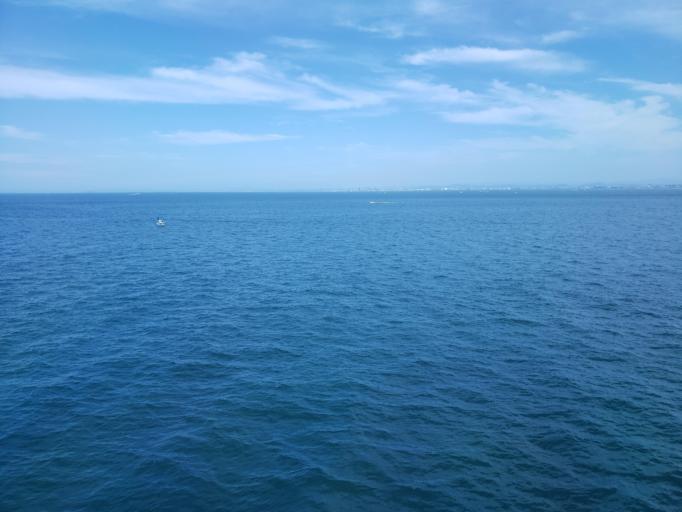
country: JP
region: Hyogo
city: Akashi
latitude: 34.6060
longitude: 134.9253
